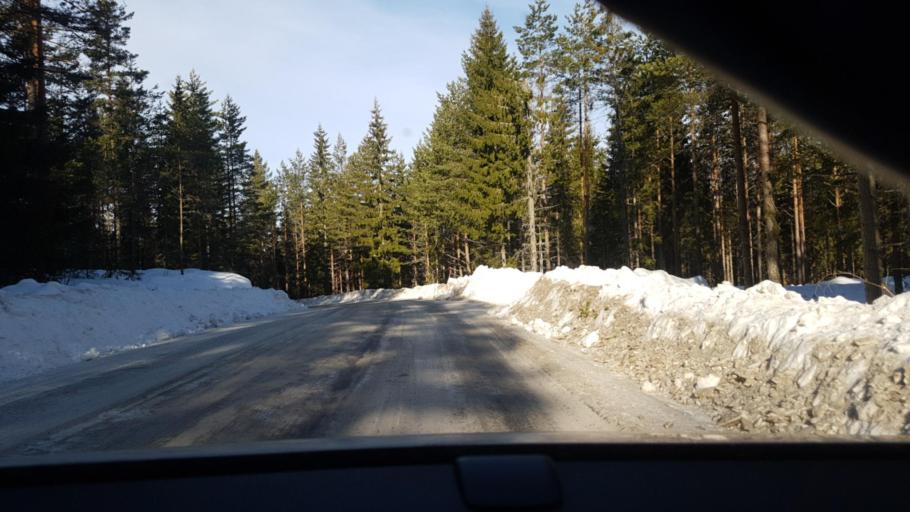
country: NO
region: Hedmark
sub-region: Eidskog
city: Skotterud
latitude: 59.8064
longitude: 12.0895
